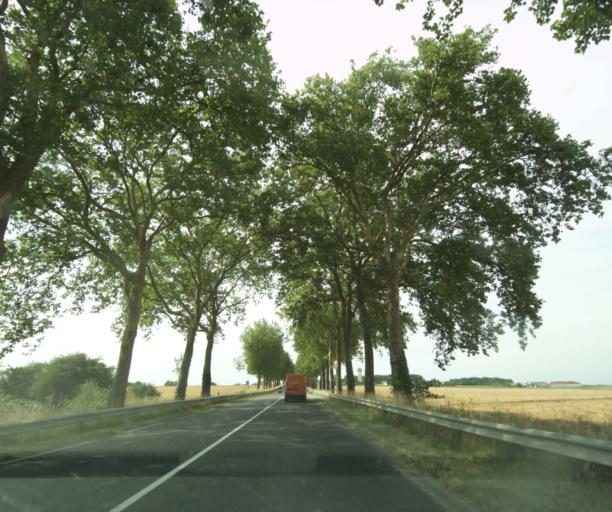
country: FR
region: Centre
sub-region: Departement d'Indre-et-Loire
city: Neuille-Pont-Pierre
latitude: 47.5375
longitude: 0.5592
